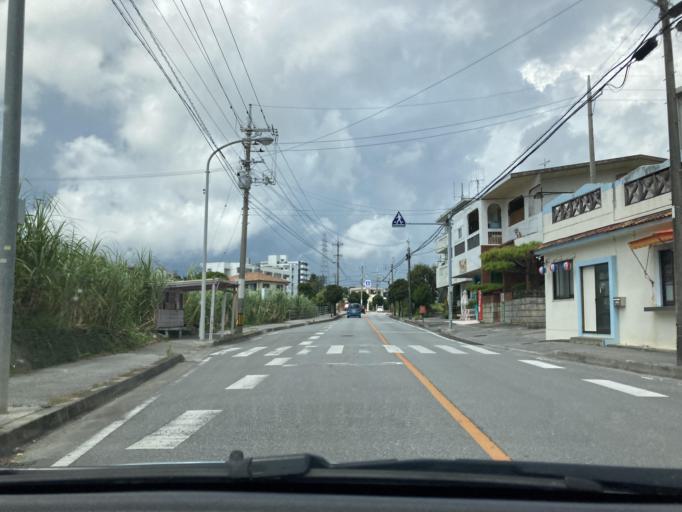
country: JP
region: Okinawa
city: Tomigusuku
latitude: 26.1645
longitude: 127.7556
